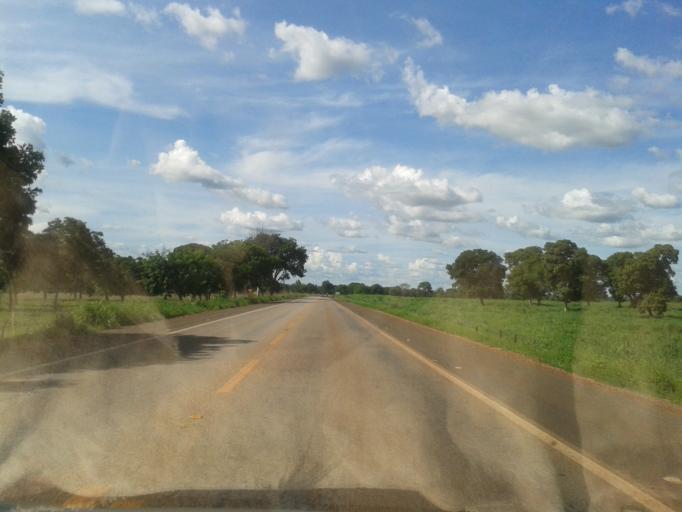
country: BR
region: Goias
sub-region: Mozarlandia
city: Mozarlandia
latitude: -15.0893
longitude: -50.6221
